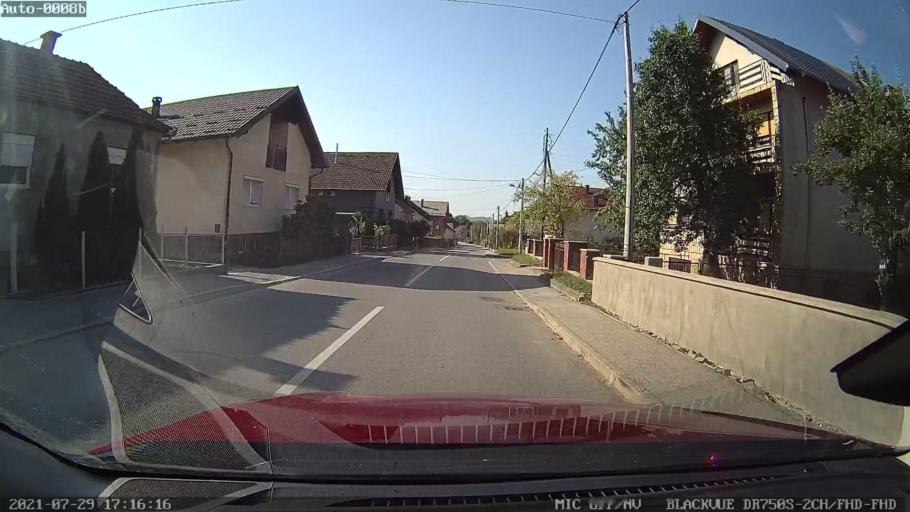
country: HR
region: Varazdinska
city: Ivanec
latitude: 46.2134
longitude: 16.1283
